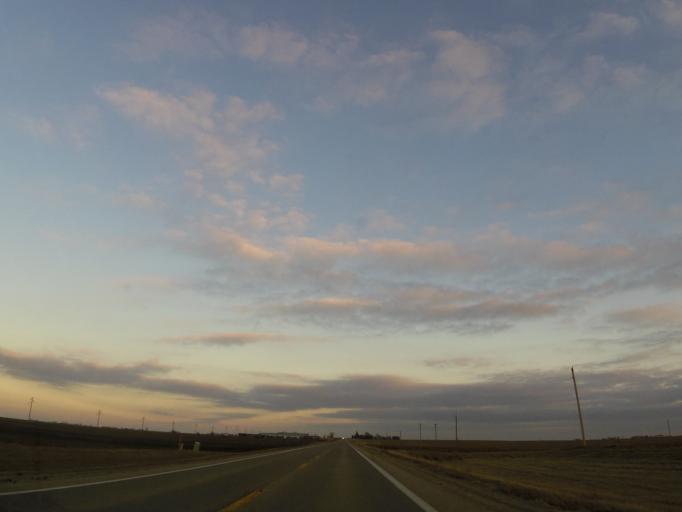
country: US
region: Illinois
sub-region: McLean County
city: Gridley
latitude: 40.7387
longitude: -88.9410
